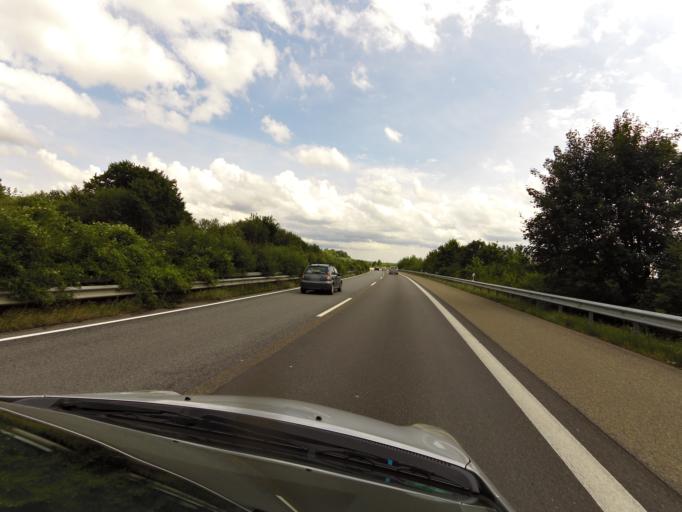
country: DE
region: Rheinland-Pfalz
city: Kleinsteinhausen
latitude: 49.2200
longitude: 7.4431
